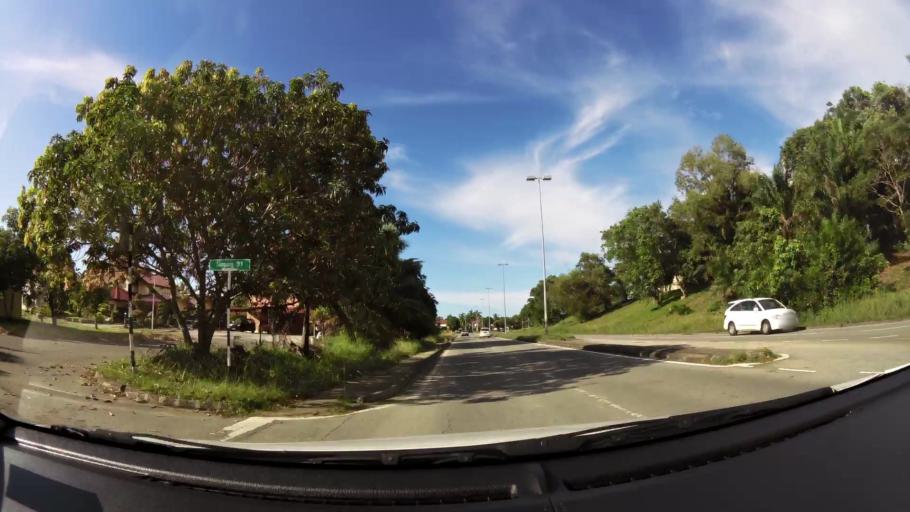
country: BN
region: Brunei and Muara
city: Bandar Seri Begawan
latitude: 4.9702
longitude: 114.9650
